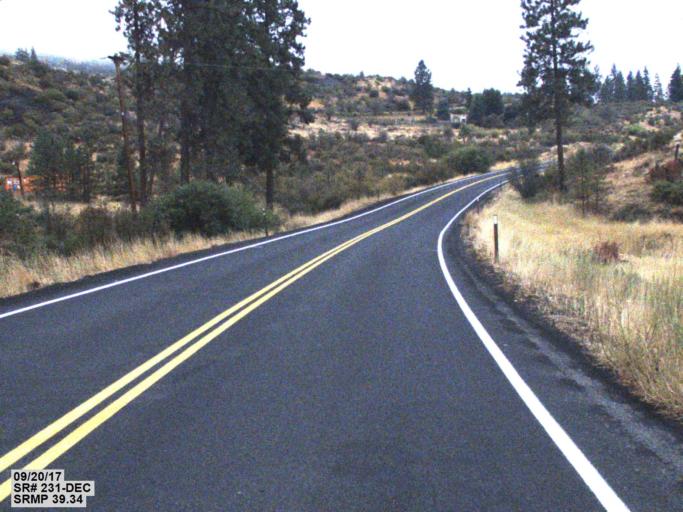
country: US
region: Washington
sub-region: Spokane County
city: Fairchild Air Force Base
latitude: 47.7797
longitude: -117.8885
